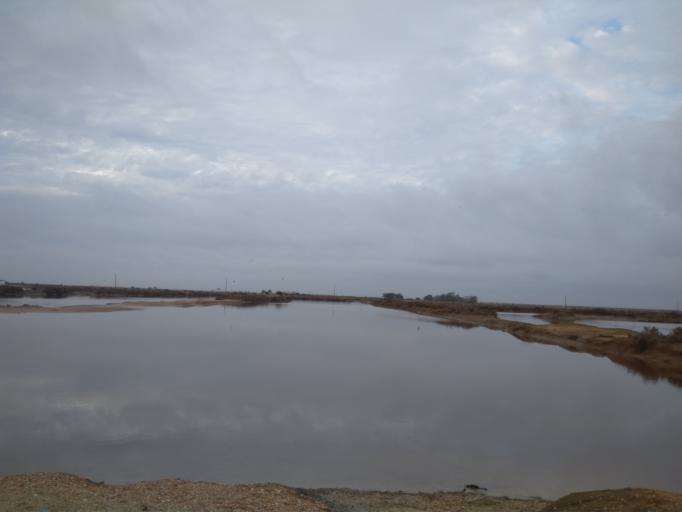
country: PT
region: Faro
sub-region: Loule
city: Almancil
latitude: 37.0302
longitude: -7.9990
